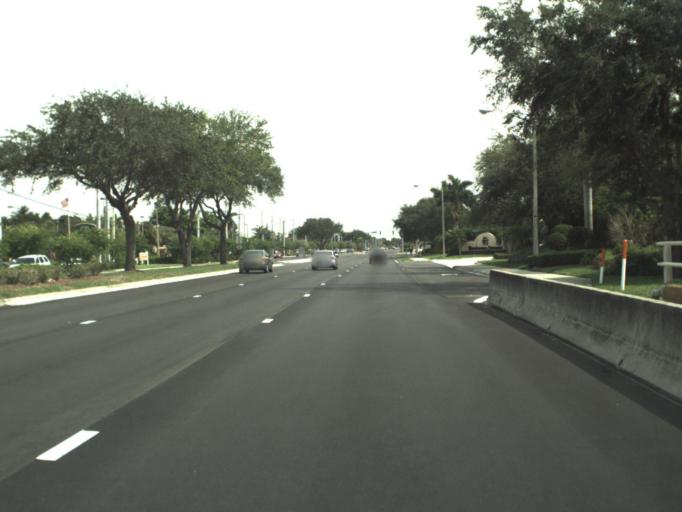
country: US
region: Florida
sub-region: Palm Beach County
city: Boynton Beach
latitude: 26.5394
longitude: -80.0906
